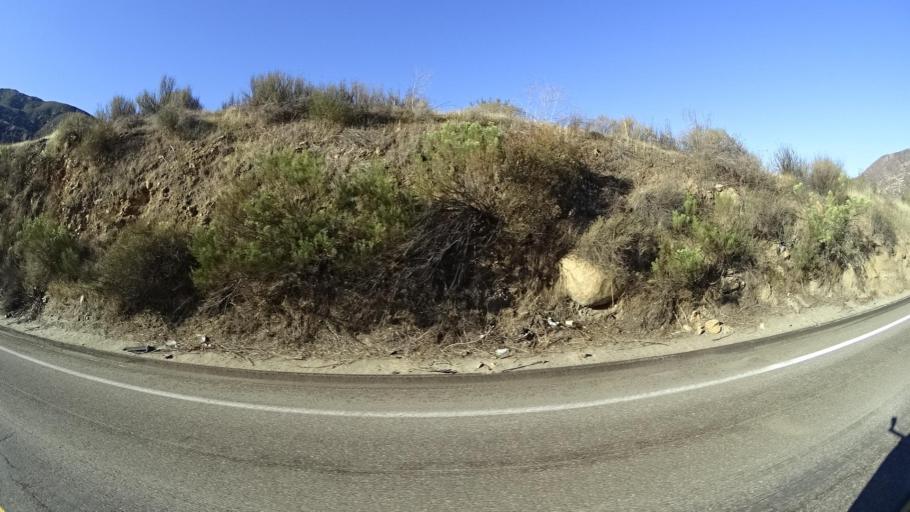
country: MX
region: Baja California
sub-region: Tecate
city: Lomas de Santa Anita
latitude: 32.6077
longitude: -116.6994
